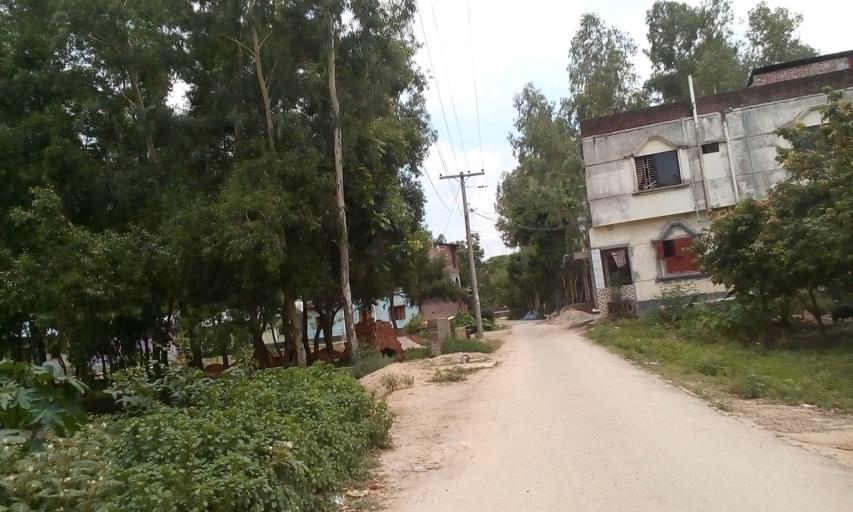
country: IN
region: West Bengal
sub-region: Dakshin Dinajpur
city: Balurghat
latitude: 25.3847
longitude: 88.9957
